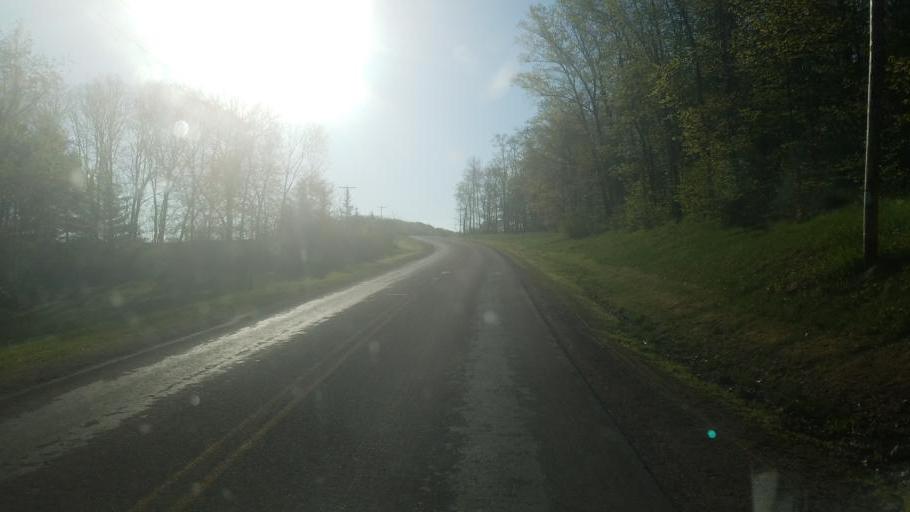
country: US
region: Wisconsin
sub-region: Vernon County
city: Hillsboro
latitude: 43.5907
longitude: -90.3834
